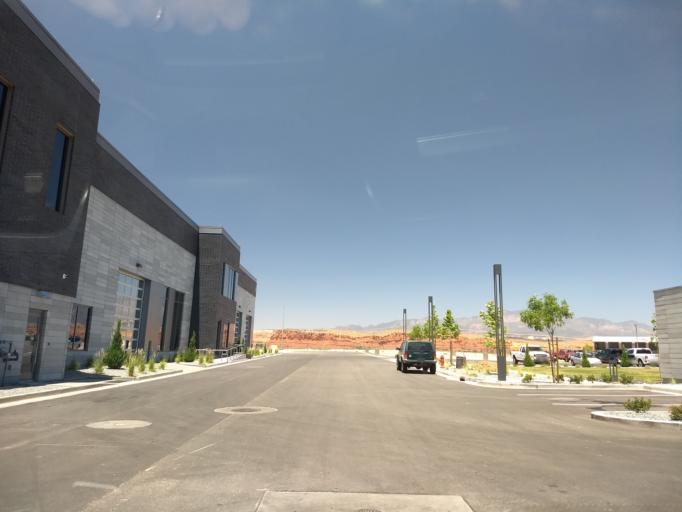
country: US
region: Utah
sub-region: Washington County
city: Saint George
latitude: 37.0985
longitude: -113.5924
